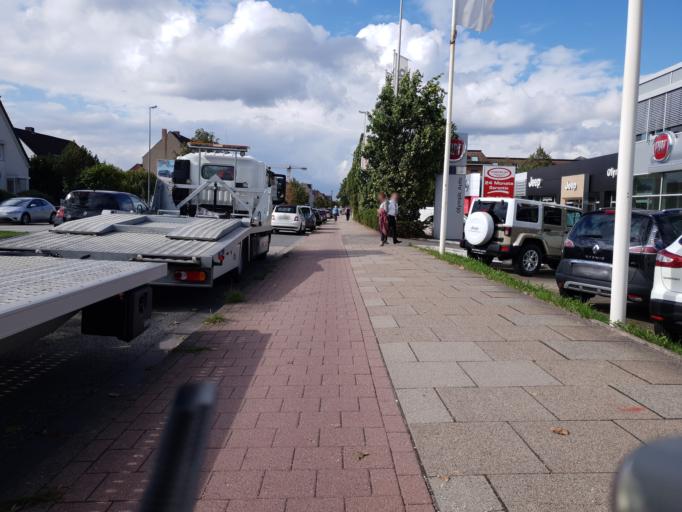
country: DE
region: Schleswig-Holstein
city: Kronshagen
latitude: 54.3404
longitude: 10.1034
